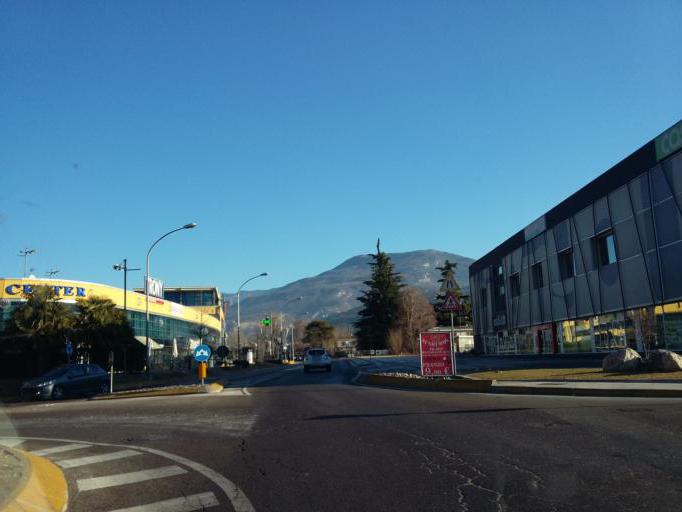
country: IT
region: Trentino-Alto Adige
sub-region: Provincia di Trento
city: Isera
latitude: 45.8681
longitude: 11.0127
